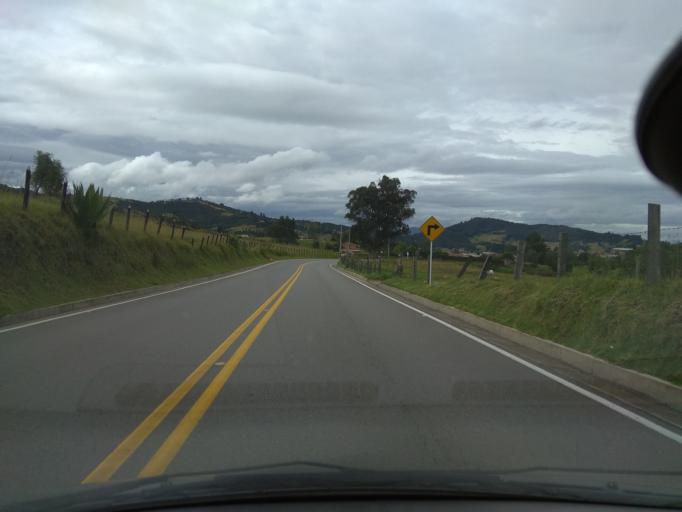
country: CO
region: Boyaca
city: Santa Rosa de Viterbo
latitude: 5.8895
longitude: -72.9785
